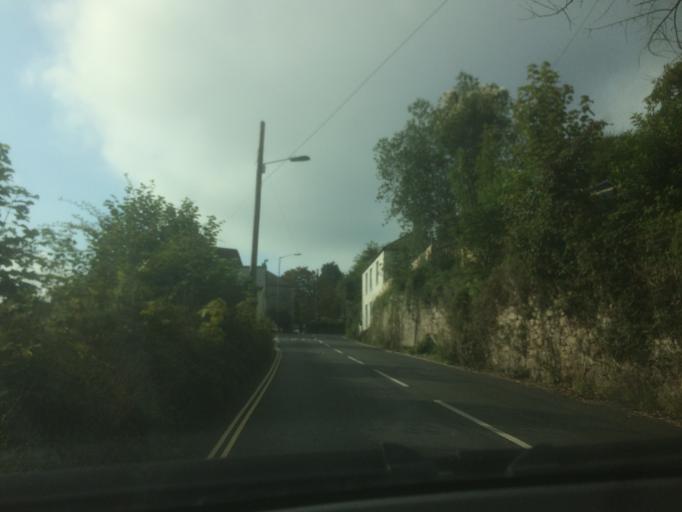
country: GB
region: England
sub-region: Cornwall
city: Gunnislake
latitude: 50.5260
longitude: -4.2127
